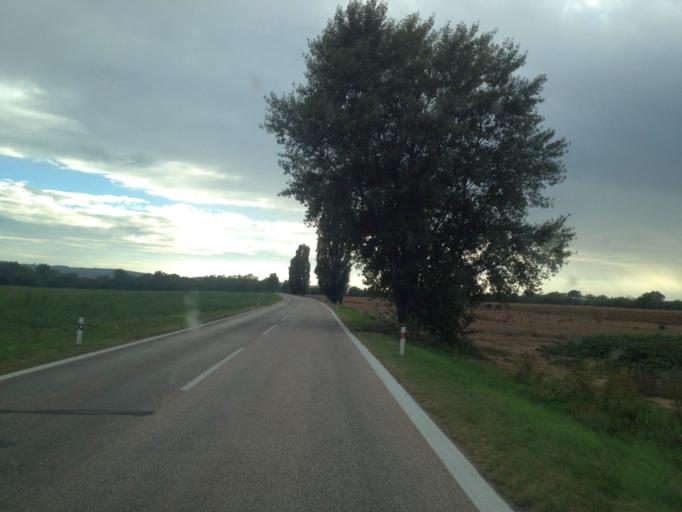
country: HU
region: Komarom-Esztergom
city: Sutto
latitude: 47.7695
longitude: 18.4273
